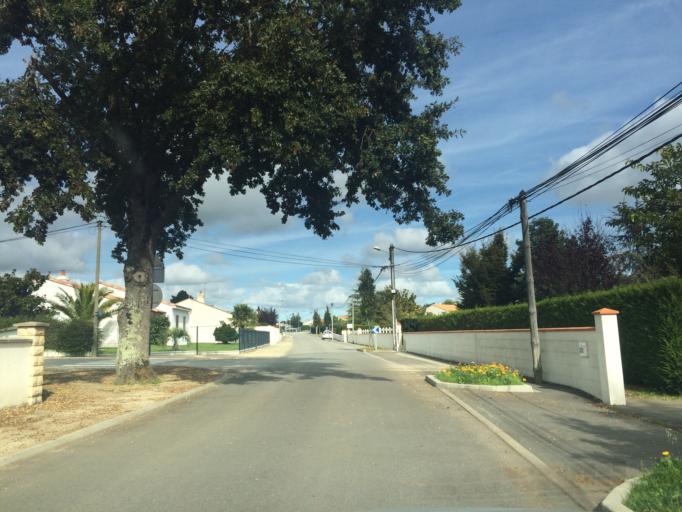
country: FR
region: Pays de la Loire
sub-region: Departement de la Loire-Atlantique
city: Chemere
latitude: 47.1161
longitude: -1.9160
